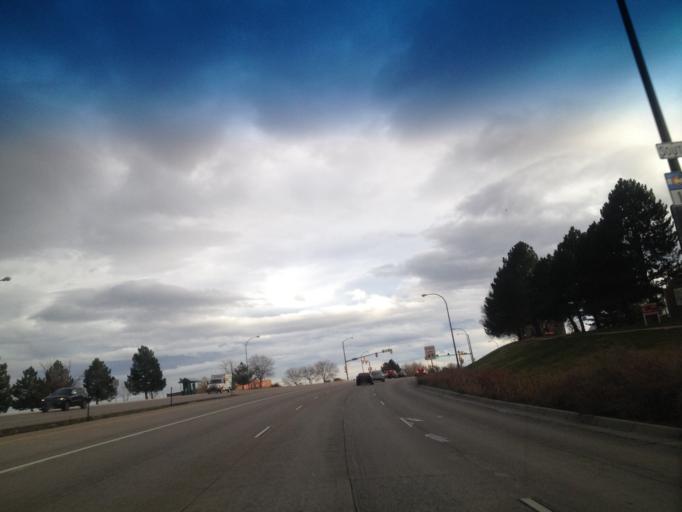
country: US
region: Colorado
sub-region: Adams County
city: Westminster
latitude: 39.8612
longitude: -105.0824
